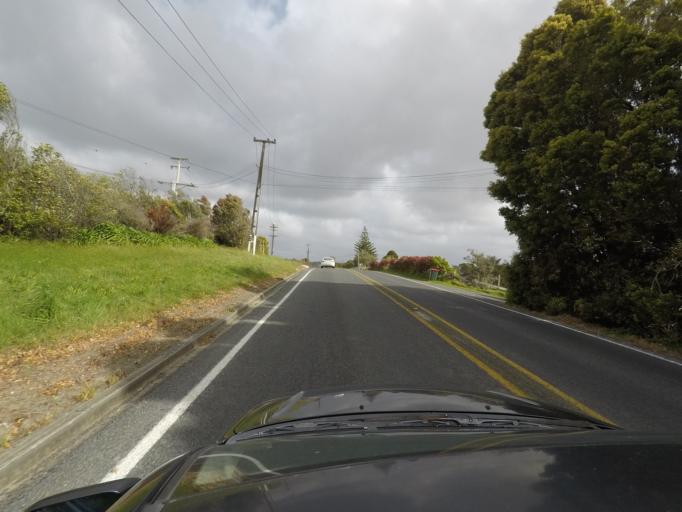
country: NZ
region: Auckland
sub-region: Auckland
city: Pakuranga
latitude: -36.9321
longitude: 174.9378
